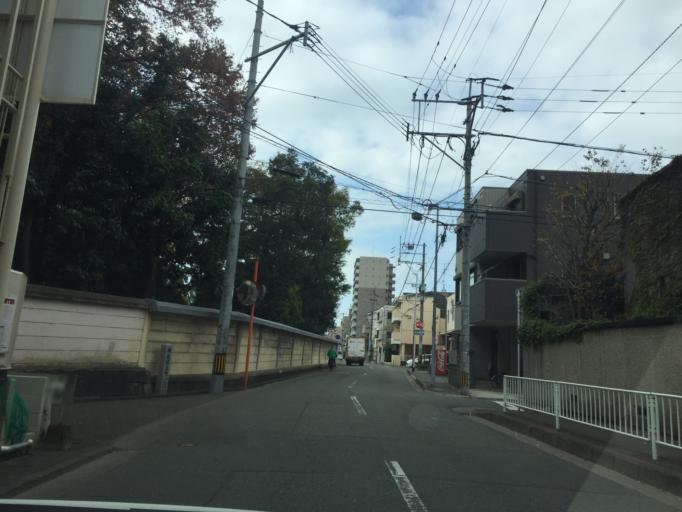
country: JP
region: Fukuoka
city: Fukuoka-shi
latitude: 33.6148
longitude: 130.4245
